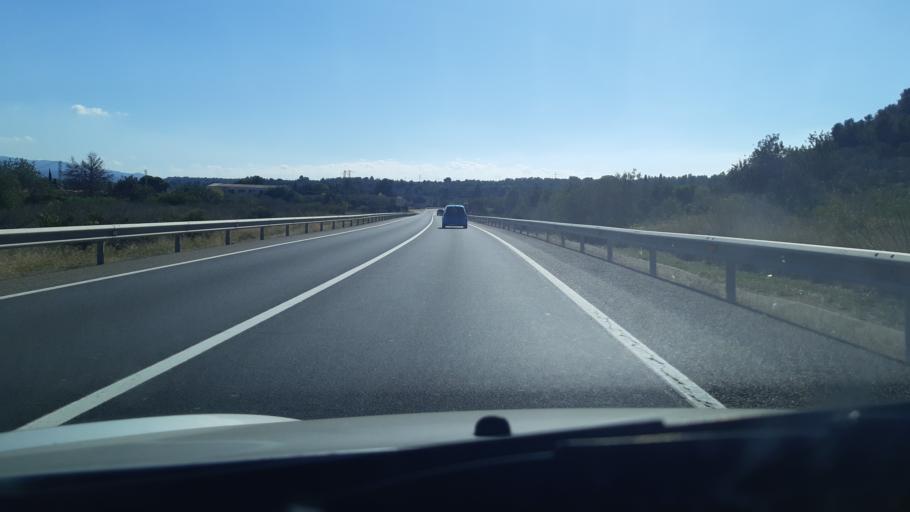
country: ES
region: Catalonia
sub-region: Provincia de Tarragona
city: Tivenys
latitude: 40.9079
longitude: 0.4832
